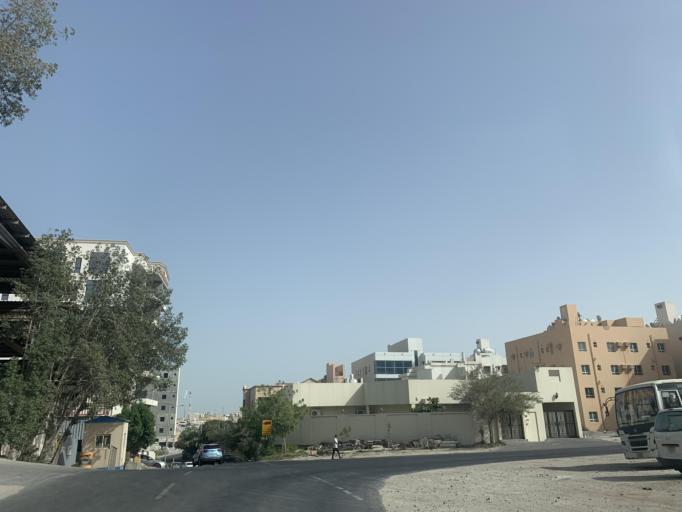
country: BH
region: Northern
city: Ar Rifa'
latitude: 26.1510
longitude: 50.5695
